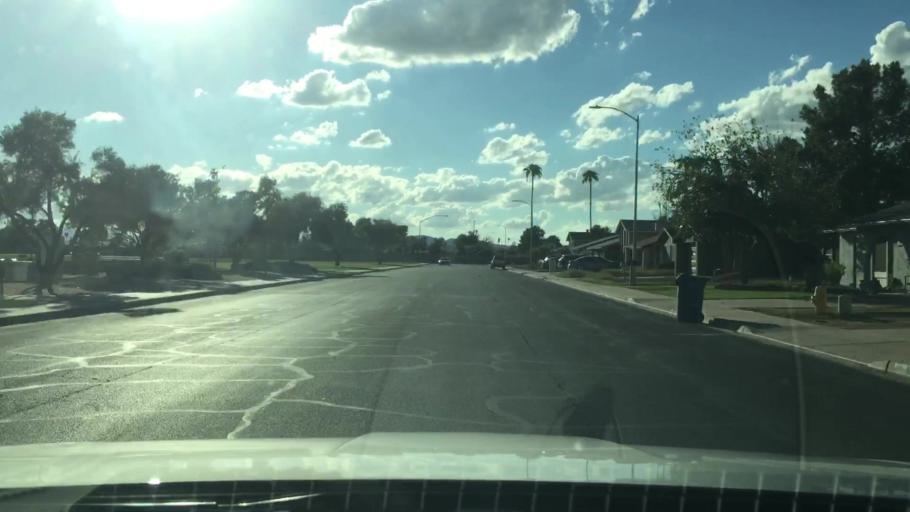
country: US
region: Arizona
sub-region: Maricopa County
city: San Carlos
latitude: 33.3589
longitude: -111.8739
